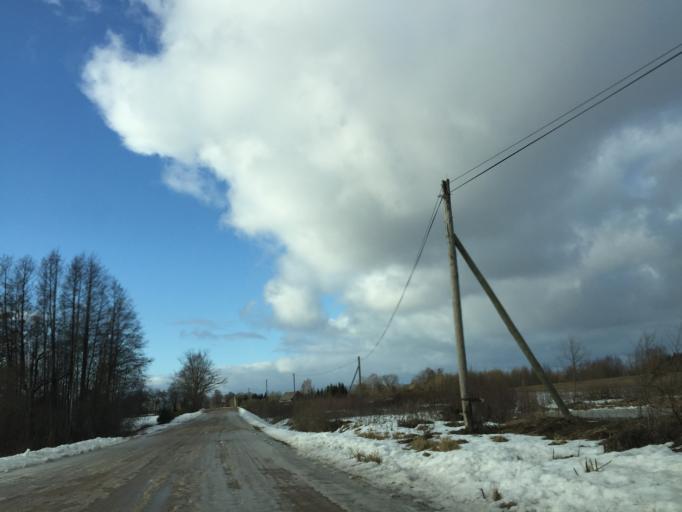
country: LV
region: Limbazu Rajons
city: Limbazi
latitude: 57.6122
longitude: 24.5904
